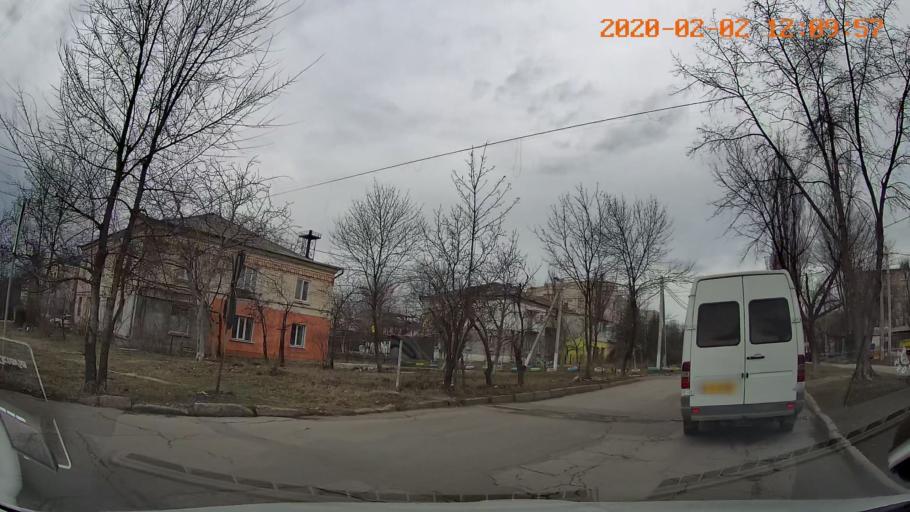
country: MD
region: Chisinau
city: Chisinau
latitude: 46.9980
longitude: 28.8057
